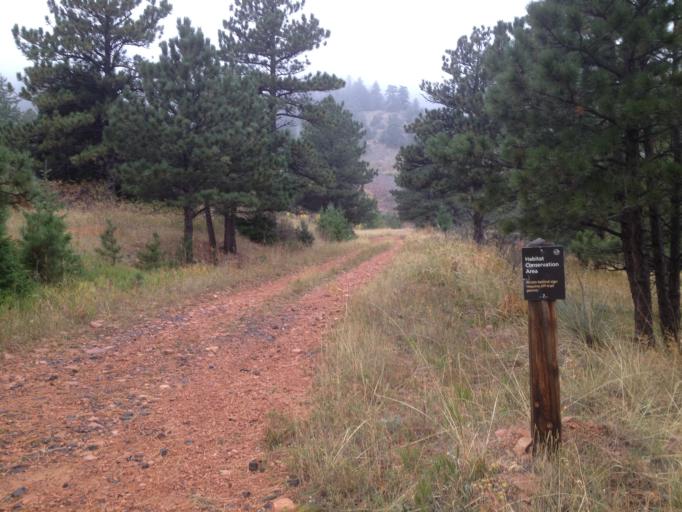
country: US
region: Colorado
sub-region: Boulder County
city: Boulder
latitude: 39.9259
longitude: -105.2782
